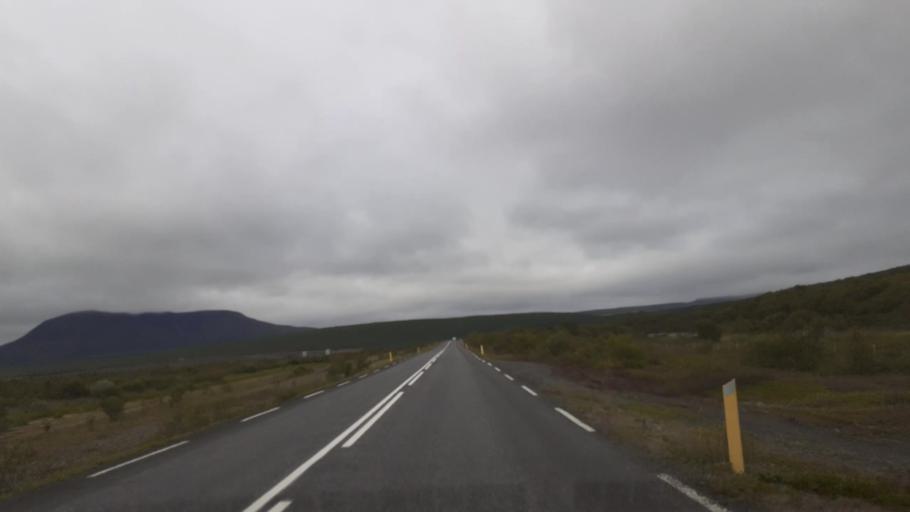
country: IS
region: Northeast
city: Husavik
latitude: 66.0309
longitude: -16.4784
